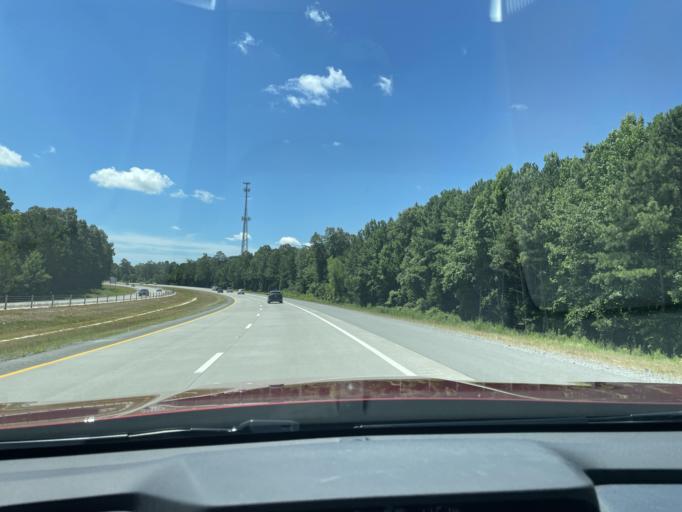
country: US
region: Arkansas
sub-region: Jefferson County
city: Sulphur Springs
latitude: 34.2022
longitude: -92.0723
